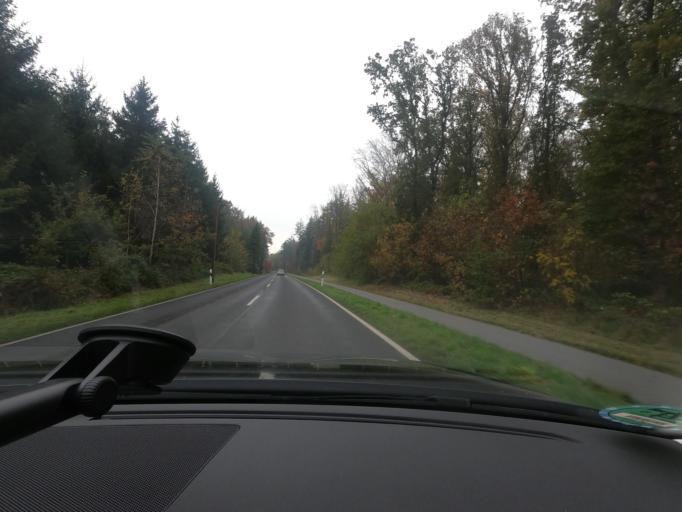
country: DE
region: North Rhine-Westphalia
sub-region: Regierungsbezirk Dusseldorf
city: Kevelaer
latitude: 51.5910
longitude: 6.2970
